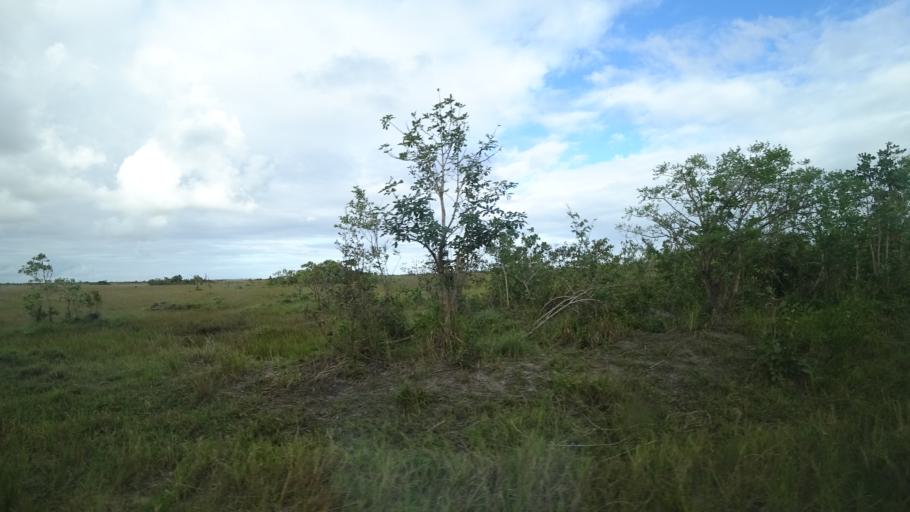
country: MZ
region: Sofala
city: Beira
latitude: -19.6645
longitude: 35.0599
